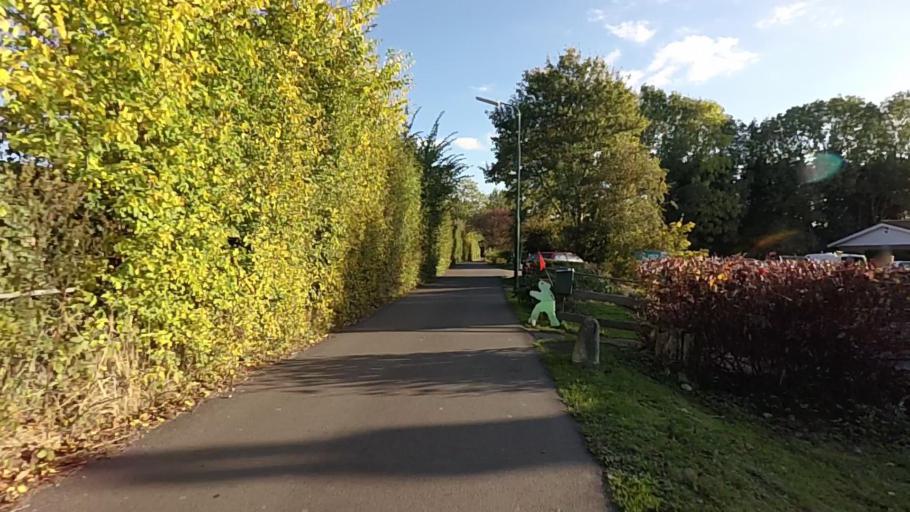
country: NL
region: North Holland
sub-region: Gemeente Amsterdam
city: Driemond
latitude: 52.2694
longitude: 5.0242
